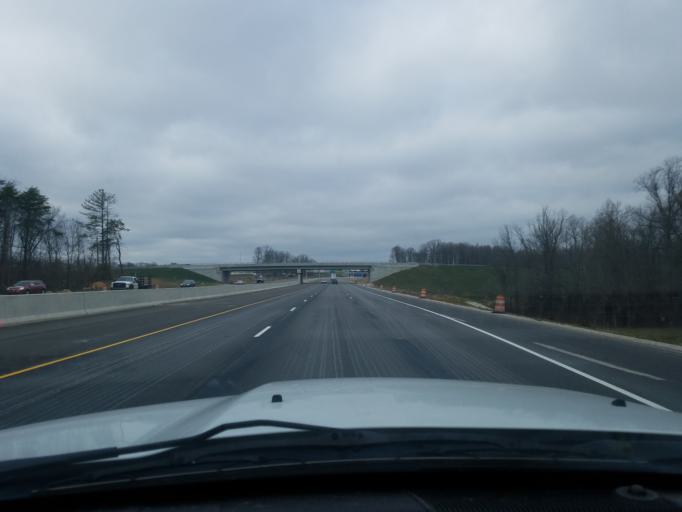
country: US
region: Indiana
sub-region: Monroe County
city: Bloomington
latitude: 39.1161
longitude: -86.5654
